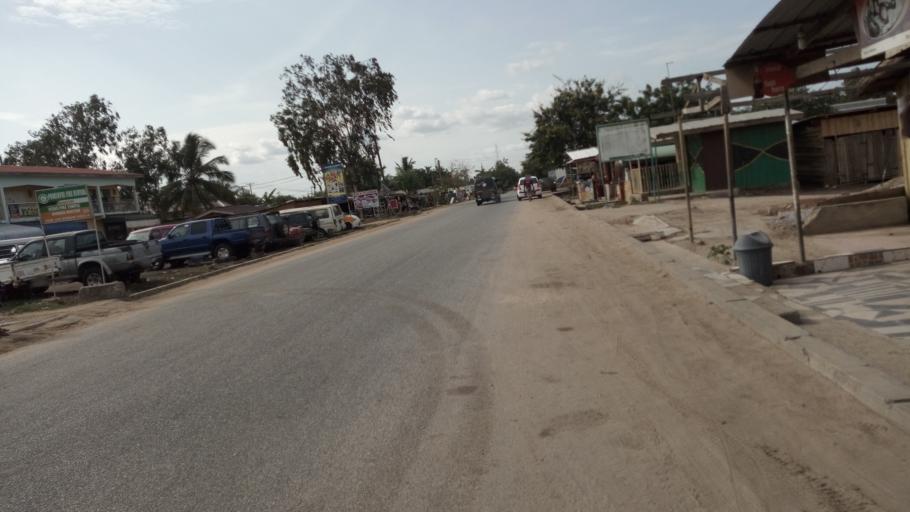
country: GH
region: Central
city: Winneba
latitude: 5.3846
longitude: -0.6432
